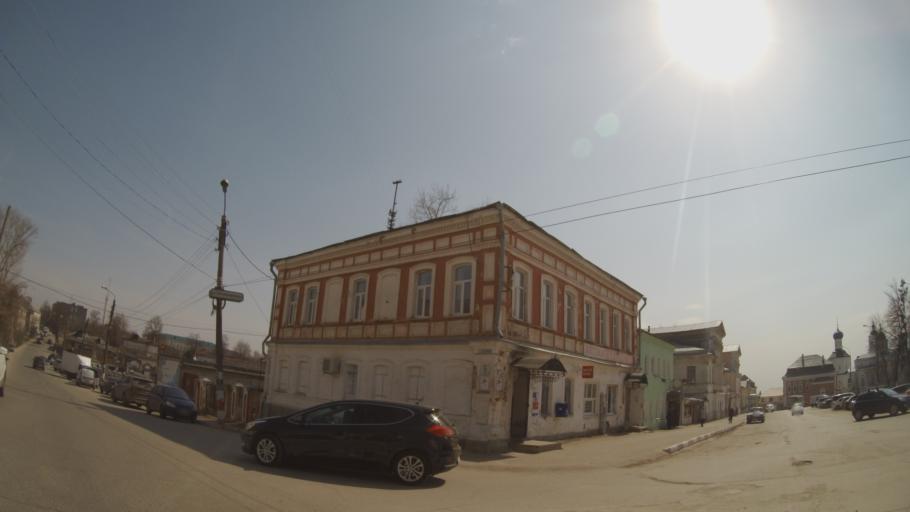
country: RU
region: Nizjnij Novgorod
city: Arzamas
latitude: 55.3875
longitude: 43.8162
